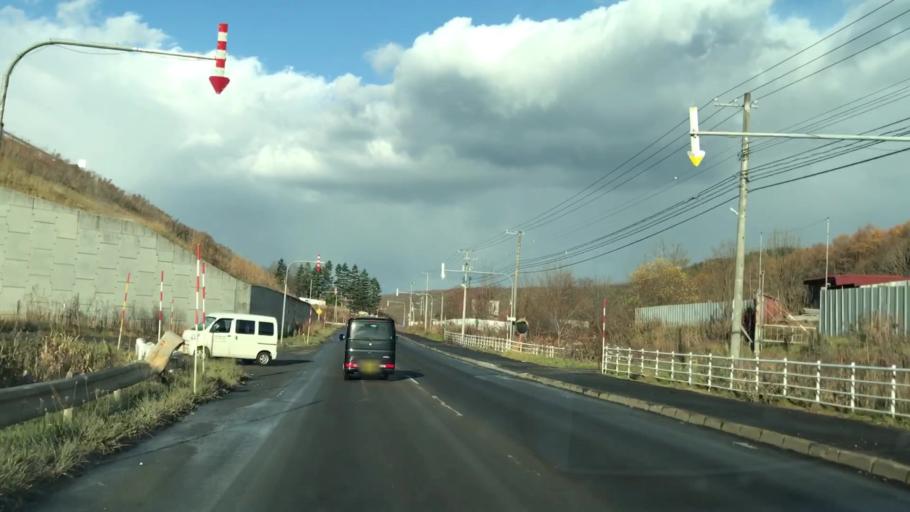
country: JP
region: Hokkaido
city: Otaru
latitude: 43.1963
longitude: 140.9527
